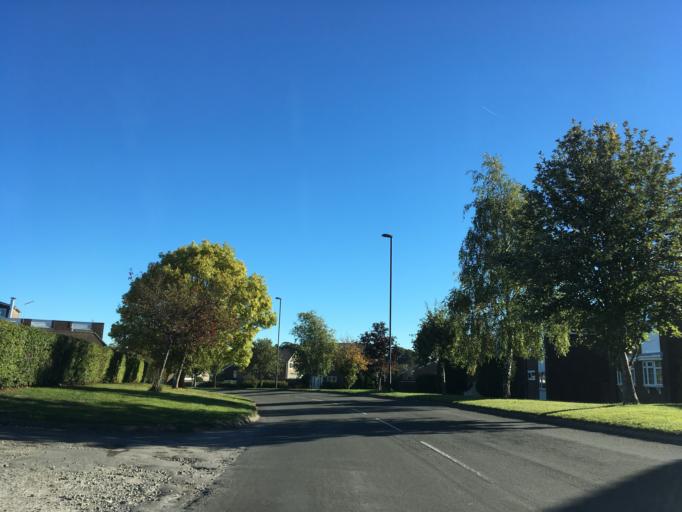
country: GB
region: England
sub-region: South Gloucestershire
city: Chipping Sodbury
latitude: 51.5312
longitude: -2.4042
